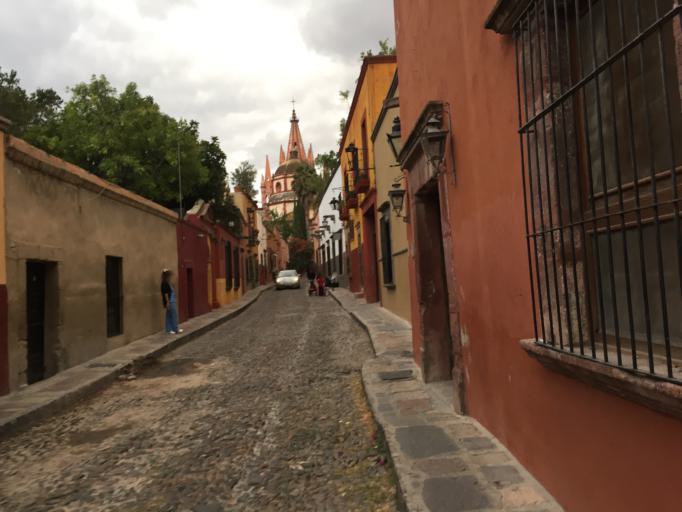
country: MX
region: Guanajuato
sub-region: San Miguel de Allende
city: San Miguel de Allende
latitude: 20.9119
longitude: -100.7436
